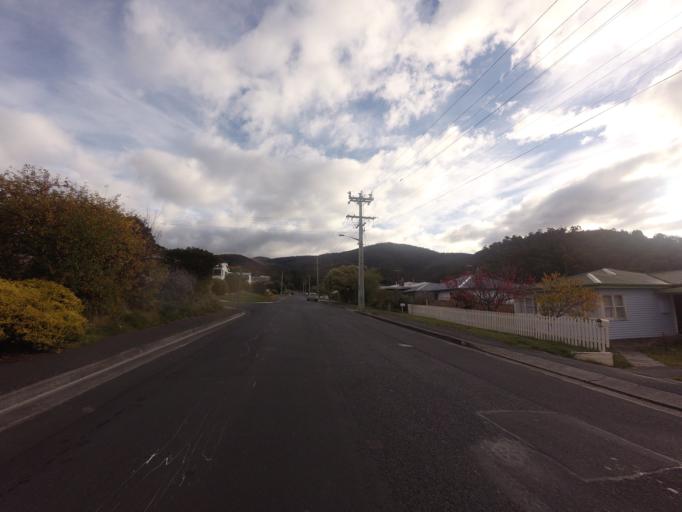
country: AU
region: Tasmania
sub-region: Glenorchy
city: Berriedale
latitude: -42.8278
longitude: 147.2610
